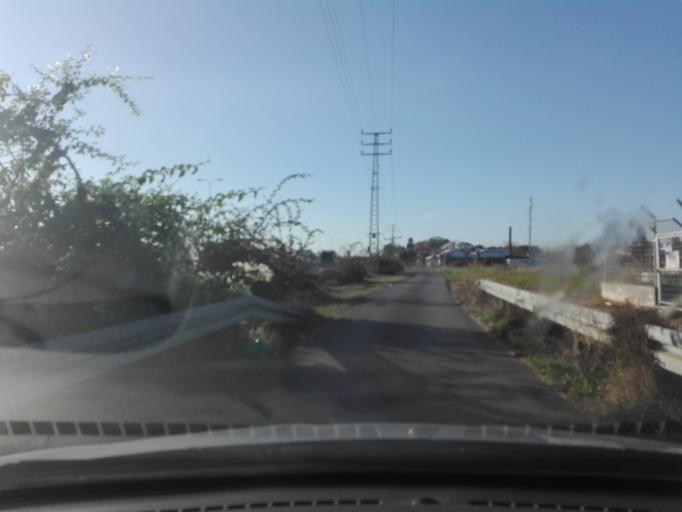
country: IL
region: Central District
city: Netanya
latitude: 32.3063
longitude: 34.8642
